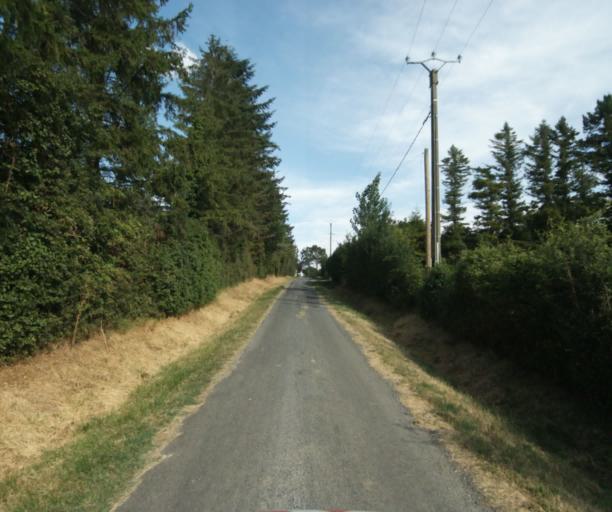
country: FR
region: Midi-Pyrenees
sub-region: Departement du Tarn
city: Puylaurens
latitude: 43.5349
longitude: 1.9889
